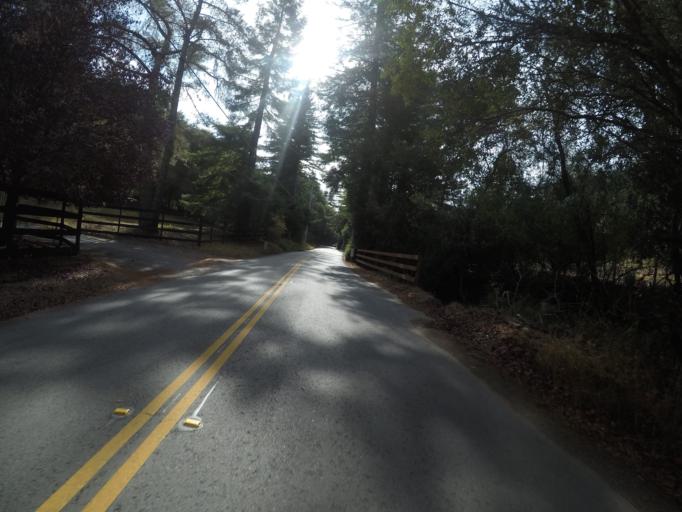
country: US
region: California
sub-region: Santa Cruz County
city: Scotts Valley
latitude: 37.0357
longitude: -121.9969
